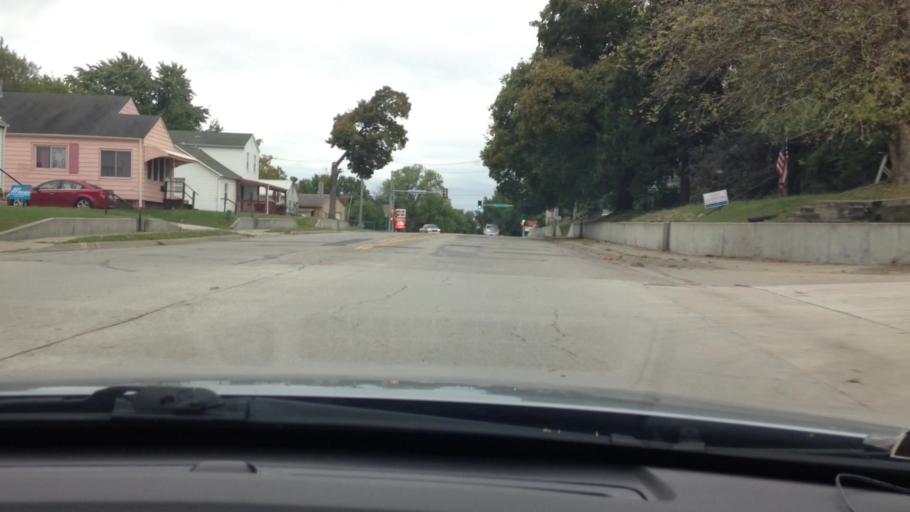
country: US
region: Kansas
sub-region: Leavenworth County
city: Leavenworth
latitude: 39.3021
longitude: -94.9276
